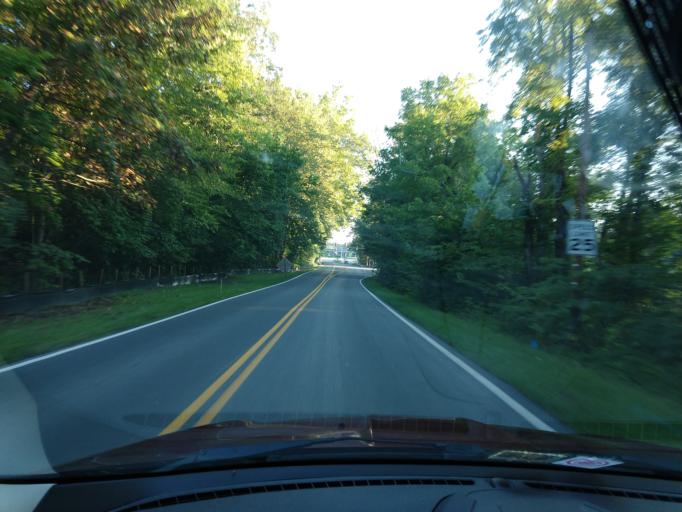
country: US
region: Virginia
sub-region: City of Covington
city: Fairlawn
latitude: 37.7685
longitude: -79.9926
